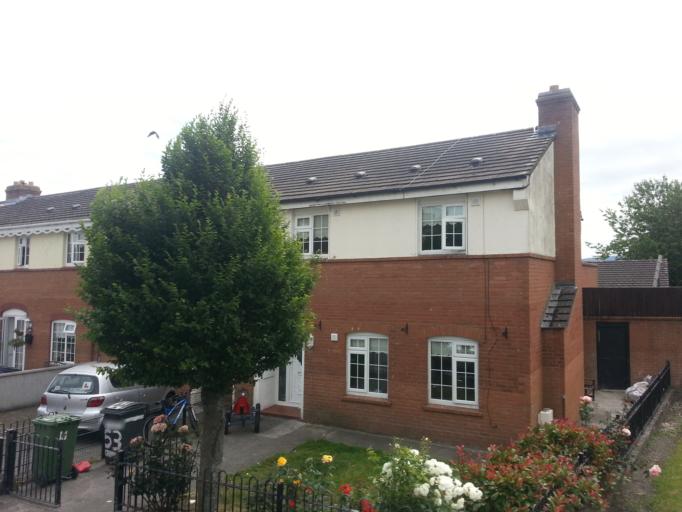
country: IE
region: Leinster
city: Rialto
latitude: 53.3506
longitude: -6.2946
